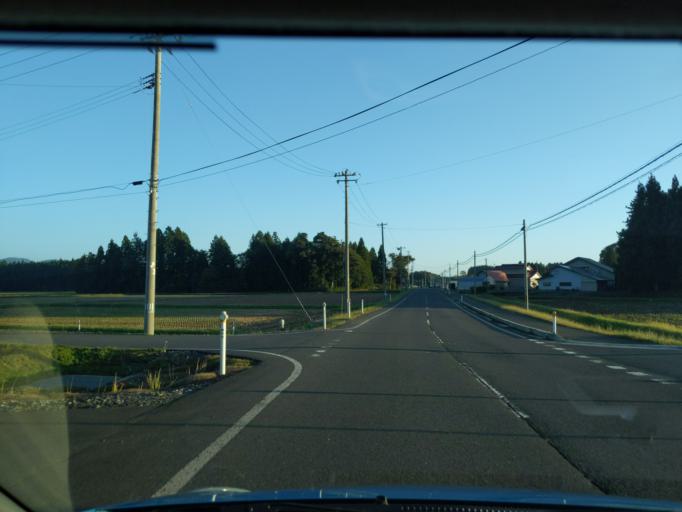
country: JP
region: Iwate
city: Mizusawa
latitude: 39.0807
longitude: 141.0927
